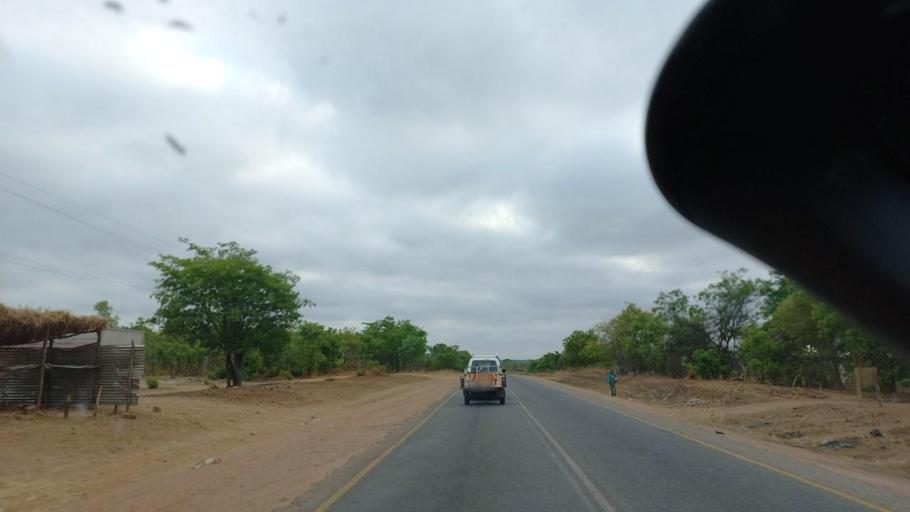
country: ZM
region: Lusaka
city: Chongwe
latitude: -15.2813
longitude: 28.7301
